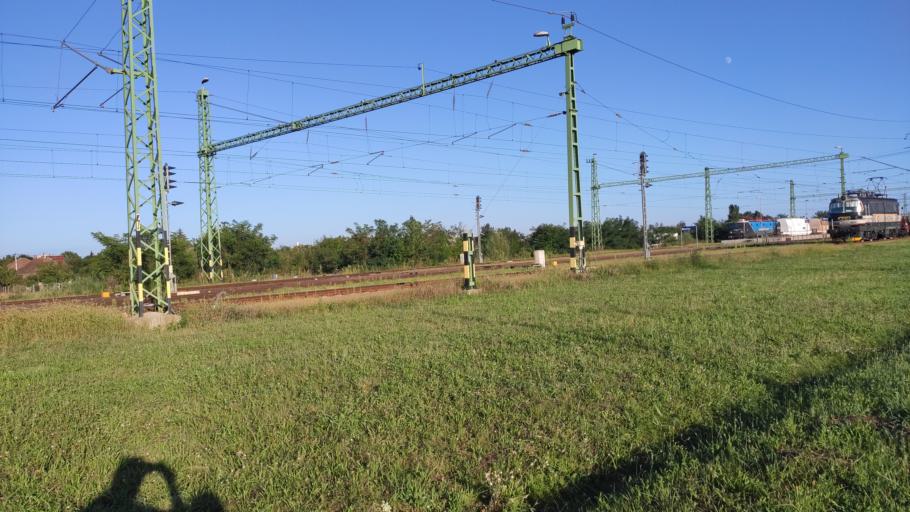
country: HU
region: Bekes
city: Mezobereny
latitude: 46.7582
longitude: 21.0372
